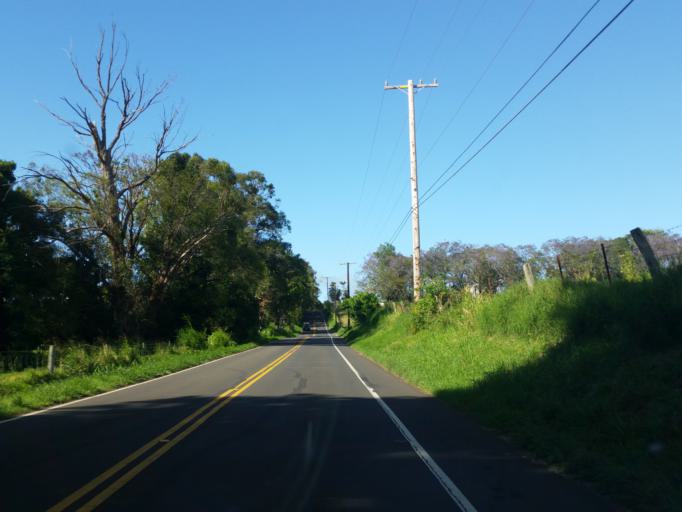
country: US
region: Hawaii
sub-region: Maui County
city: Makawao
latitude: 20.8339
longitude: -156.3128
